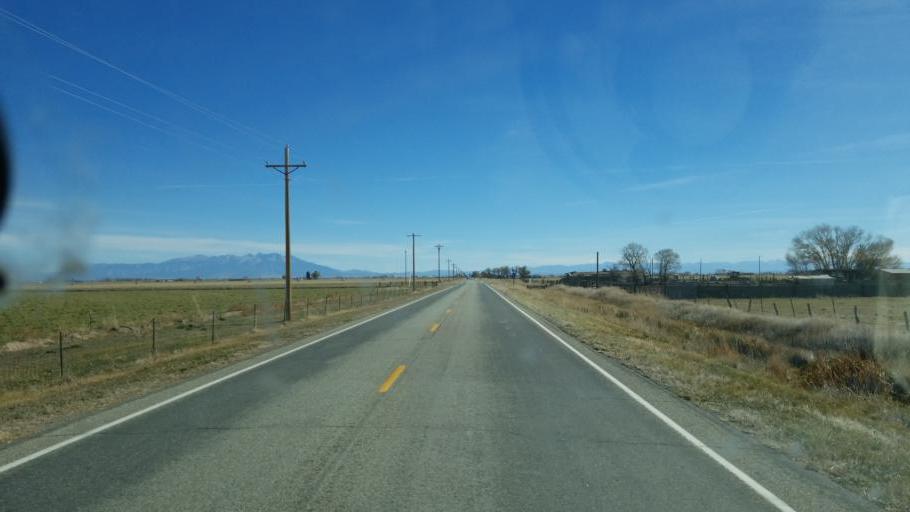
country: US
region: Colorado
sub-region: Rio Grande County
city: Monte Vista
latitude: 37.4300
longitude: -106.0965
